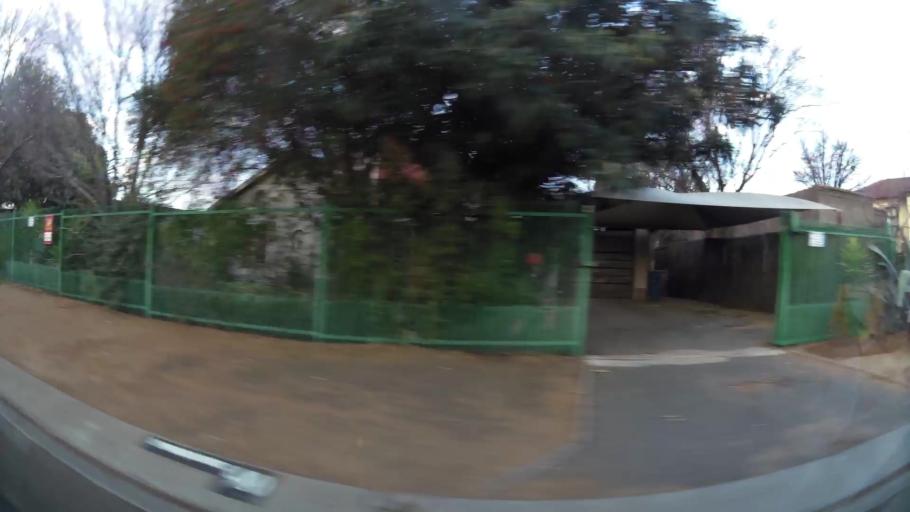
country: ZA
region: Orange Free State
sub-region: Mangaung Metropolitan Municipality
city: Bloemfontein
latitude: -29.1670
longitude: 26.1847
